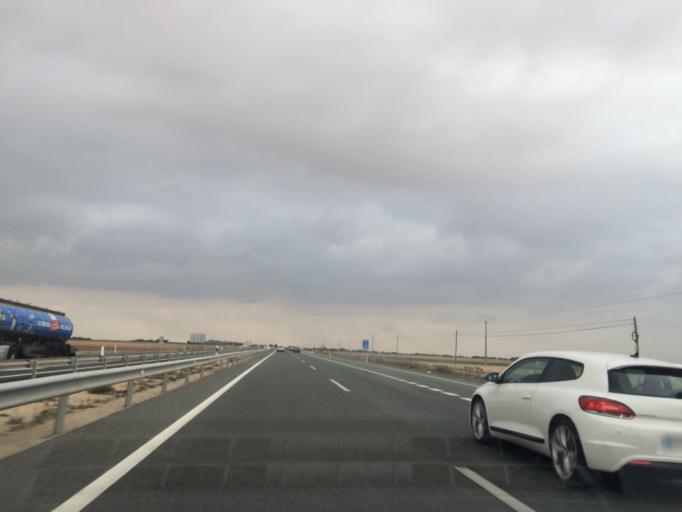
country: ES
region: Castille-La Mancha
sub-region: Province of Toledo
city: Tembleque
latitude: 39.6516
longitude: -3.5147
